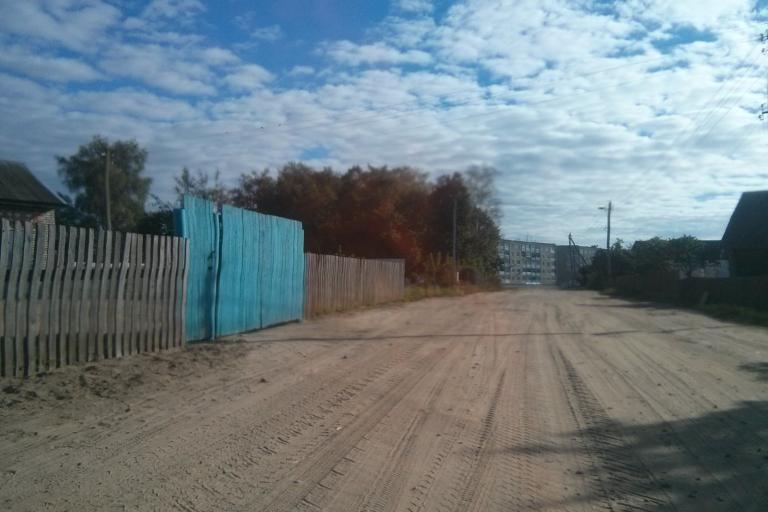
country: BY
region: Minsk
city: Chervyen'
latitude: 53.7189
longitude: 28.3943
